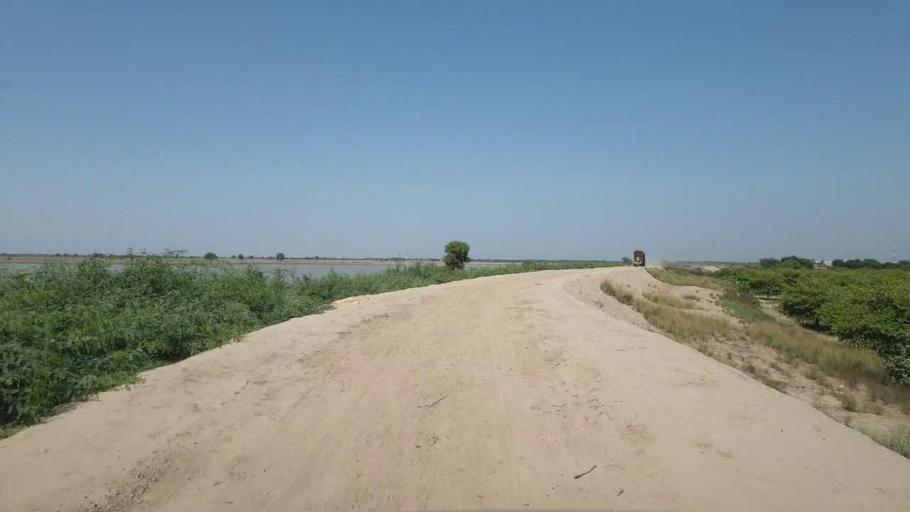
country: PK
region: Sindh
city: Matiari
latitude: 25.6377
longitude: 68.4863
